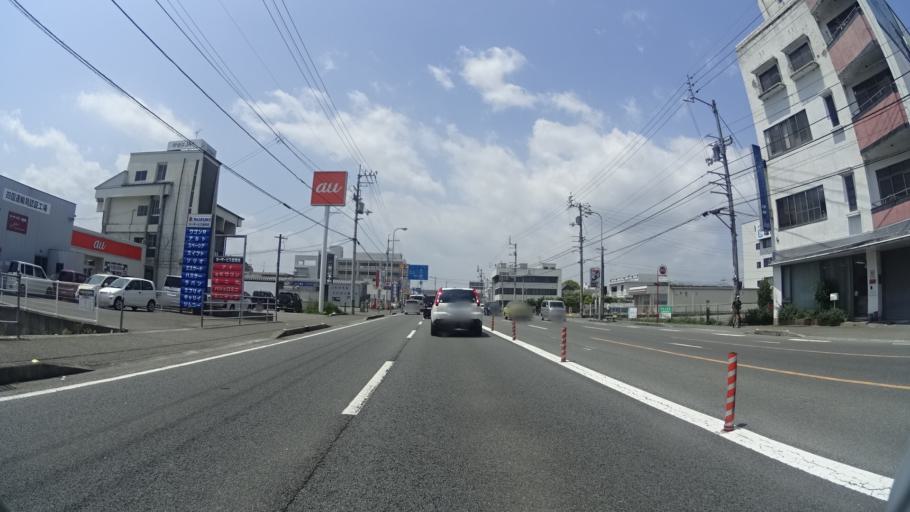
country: JP
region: Tokushima
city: Tokushima-shi
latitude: 34.0720
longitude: 134.5046
